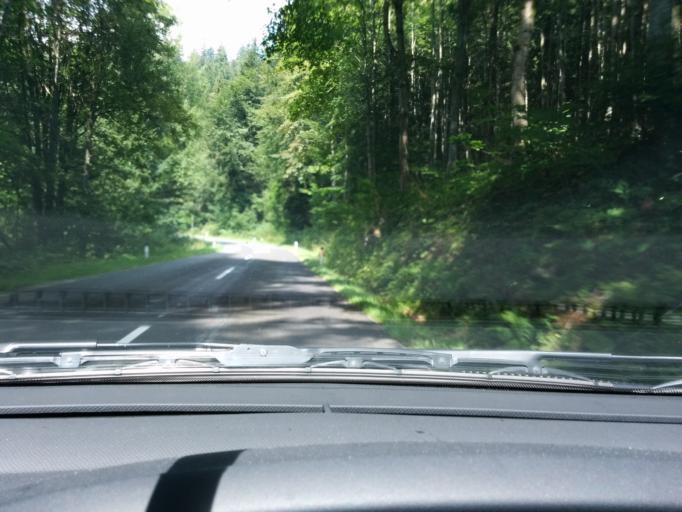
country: AT
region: Upper Austria
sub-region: Politischer Bezirk Rohrbach
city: Ulrichsberg
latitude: 48.7221
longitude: 13.8952
